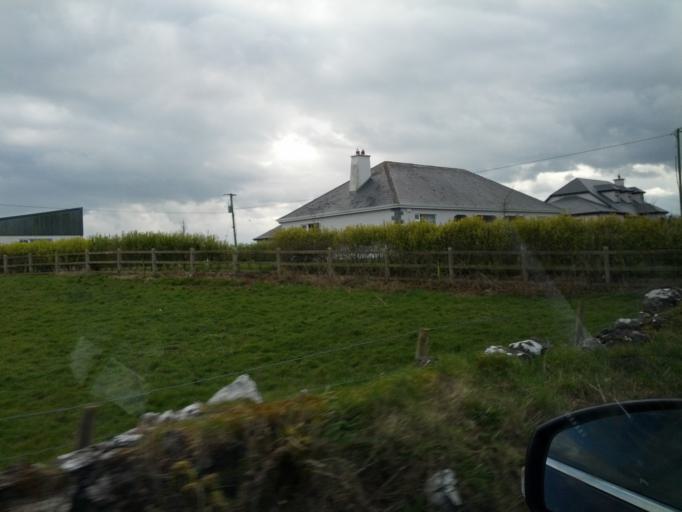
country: IE
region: Connaught
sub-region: County Galway
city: Athenry
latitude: 53.4886
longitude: -8.5869
